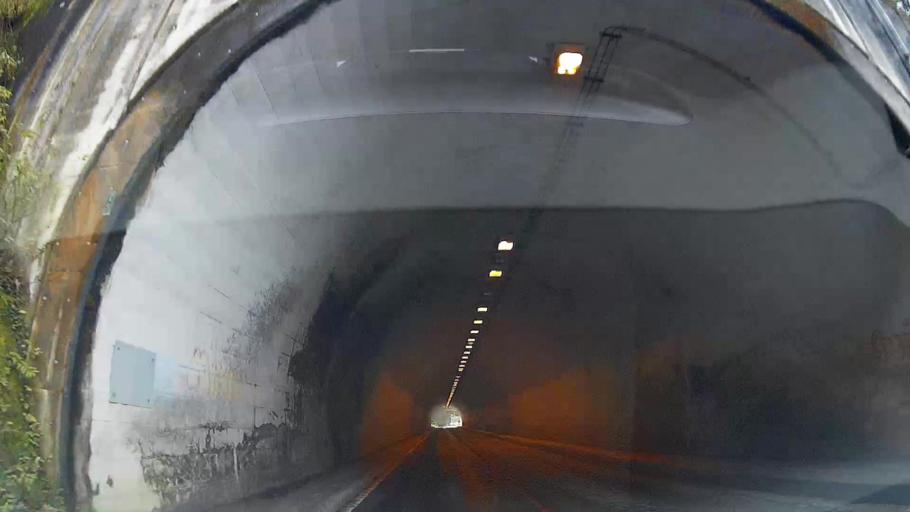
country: JP
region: Saitama
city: Chichibu
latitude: 35.9559
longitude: 139.0564
